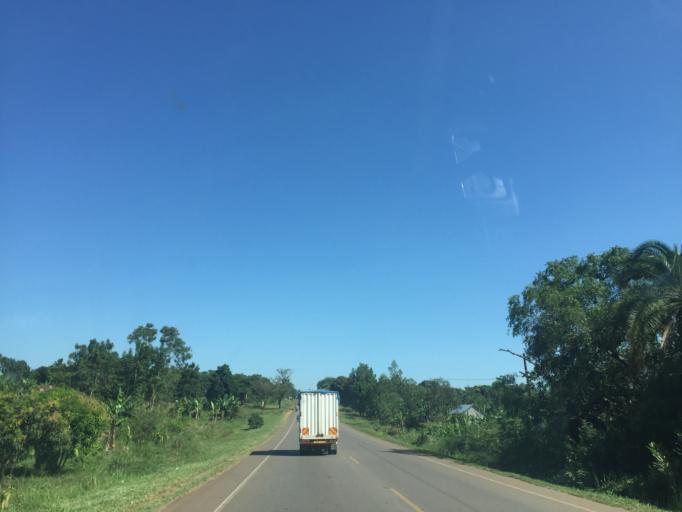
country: UG
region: Central Region
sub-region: Luwero District
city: Luwero
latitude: 0.8048
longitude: 32.5062
